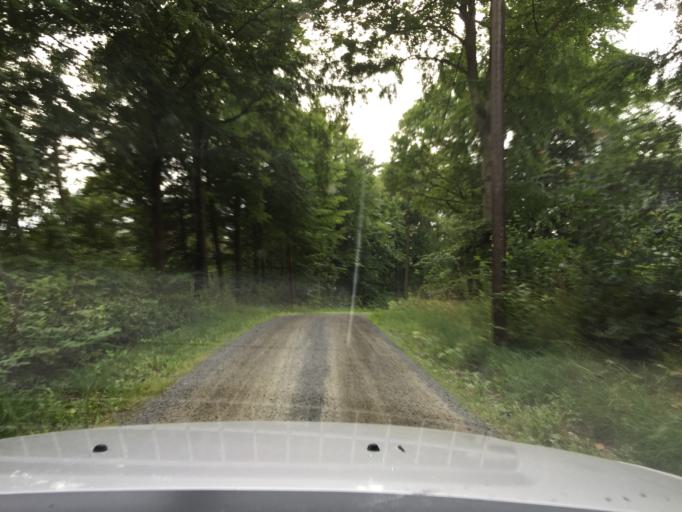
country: SE
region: Skane
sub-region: Hassleholms Kommun
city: Sosdala
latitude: 56.0103
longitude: 13.6554
